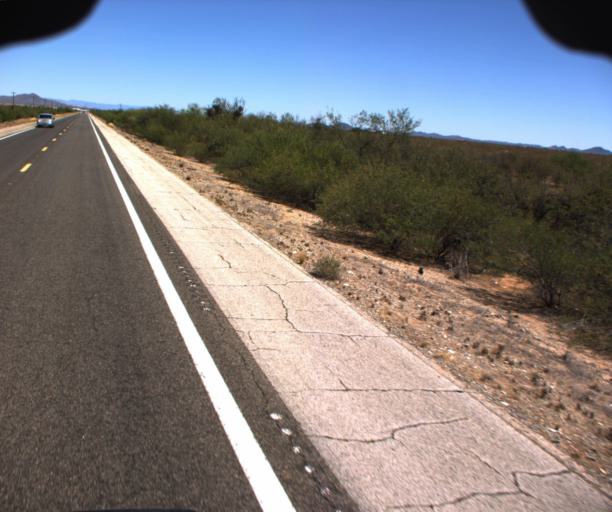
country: US
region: Arizona
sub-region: La Paz County
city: Salome
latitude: 33.9309
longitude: -113.2173
